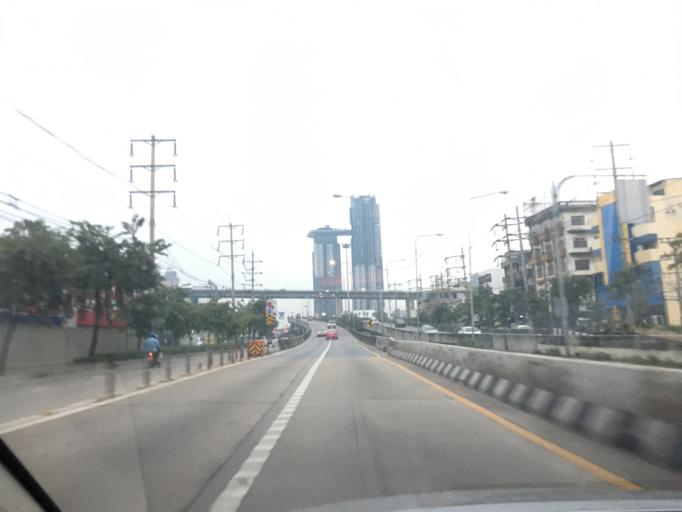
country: TH
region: Bangkok
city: Rat Burana
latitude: 13.6838
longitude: 100.5236
